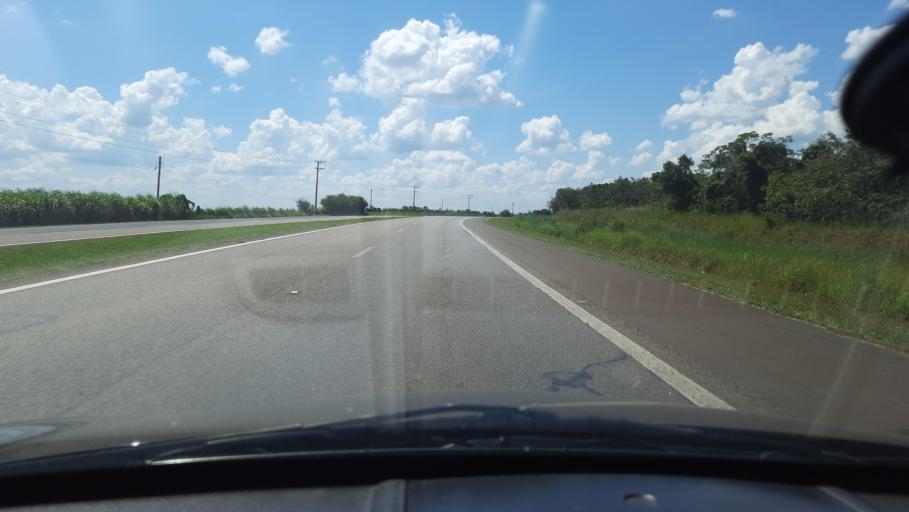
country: BR
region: Sao Paulo
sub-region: Casa Branca
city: Casa Branca
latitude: -21.7107
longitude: -47.0848
